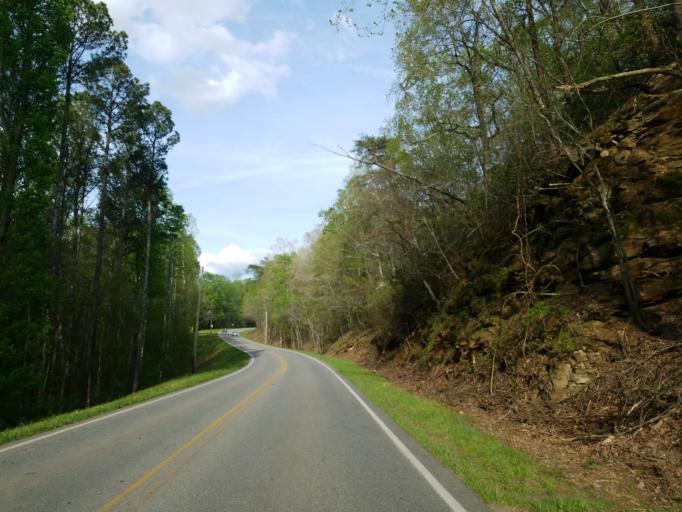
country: US
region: Georgia
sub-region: Pickens County
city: Jasper
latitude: 34.4637
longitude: -84.3722
